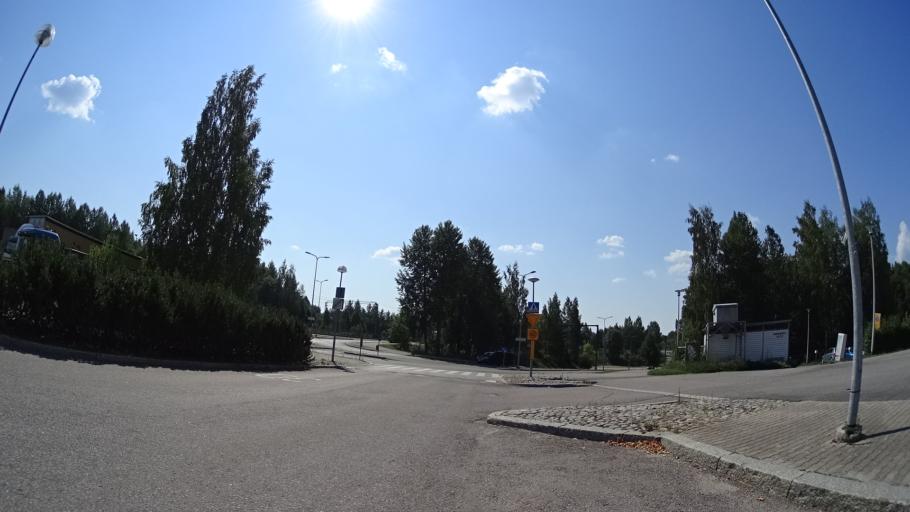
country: FI
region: Uusimaa
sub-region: Helsinki
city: Kerava
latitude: 60.3481
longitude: 25.0751
